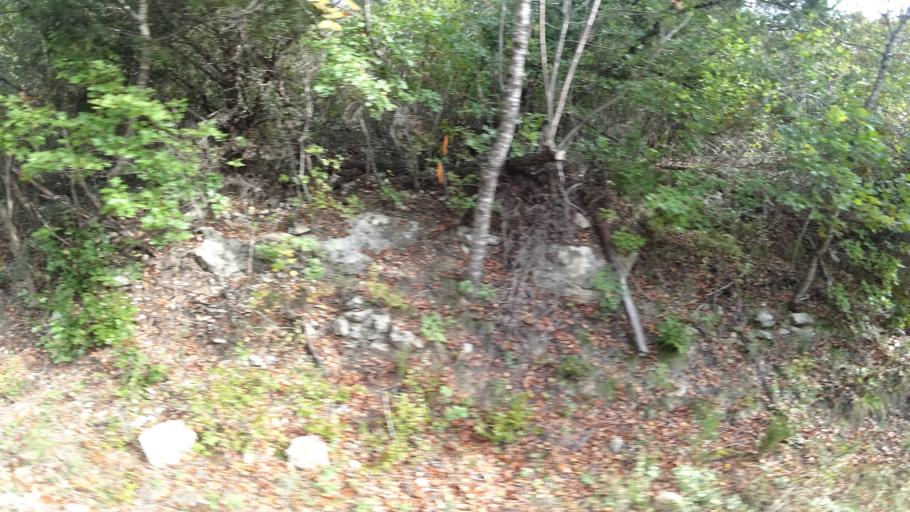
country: US
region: Texas
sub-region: Travis County
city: Hudson Bend
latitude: 30.3866
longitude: -97.9214
